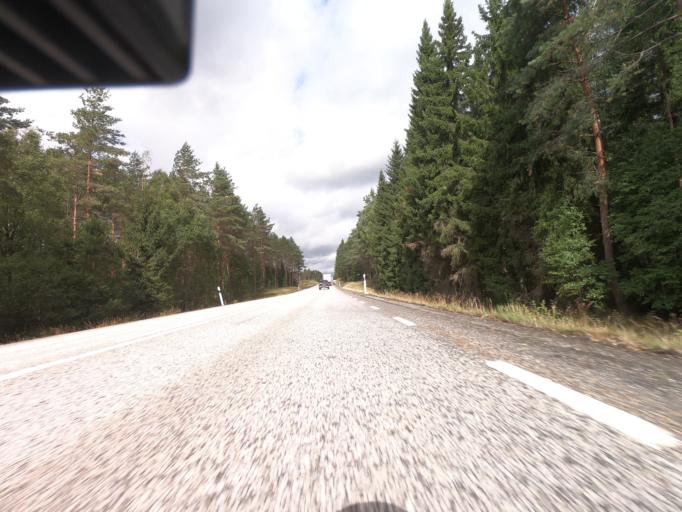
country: SE
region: Joenkoeping
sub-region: Vaggeryds Kommun
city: Vaggeryd
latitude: 57.5619
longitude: 14.2522
